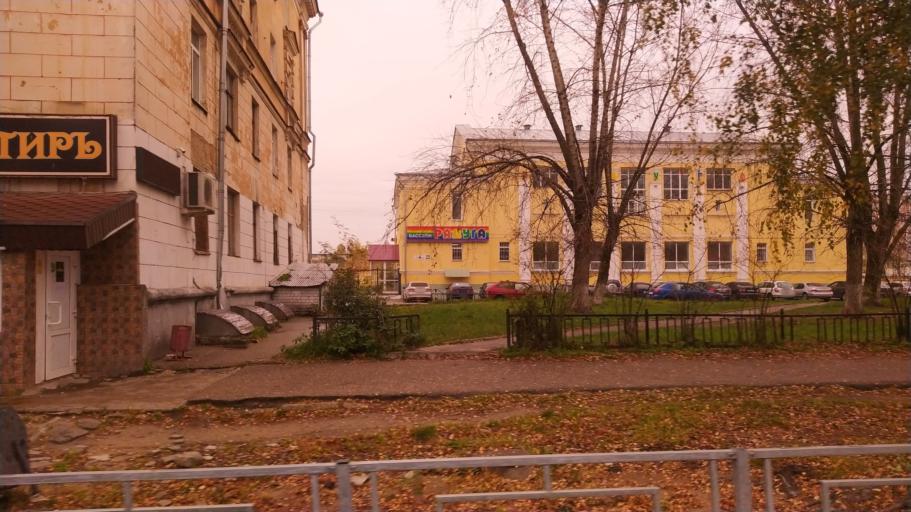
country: RU
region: Tverskaya
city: Tver
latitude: 56.8410
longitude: 35.9275
